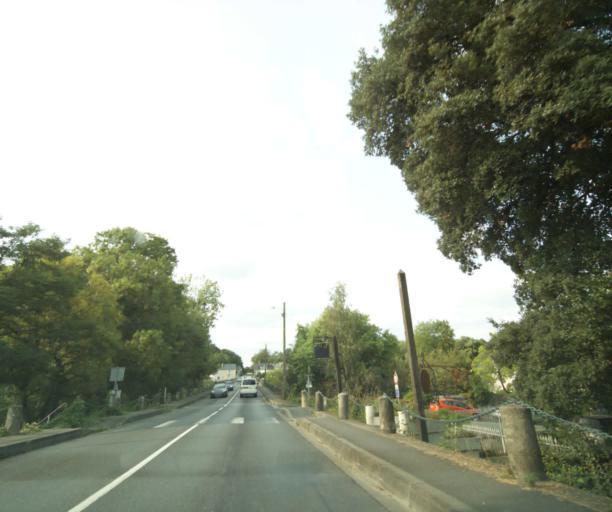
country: FR
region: Centre
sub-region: Departement d'Indre-et-Loire
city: Cormery
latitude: 47.2702
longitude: 0.8346
